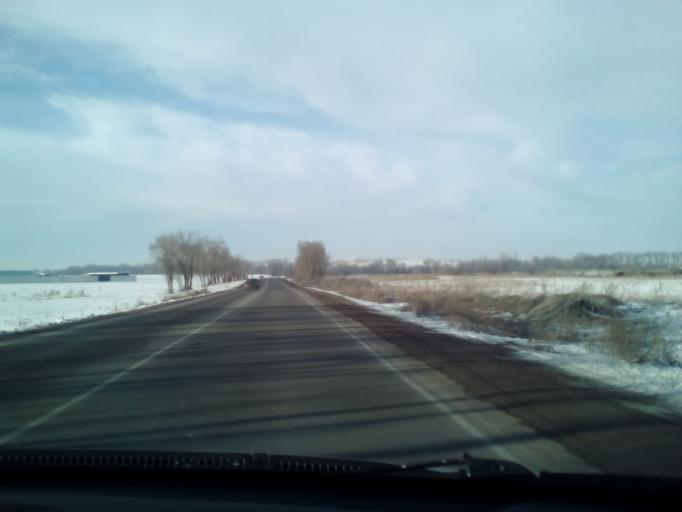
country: KZ
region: Almaty Oblysy
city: Burunday
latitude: 43.2153
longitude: 76.4142
